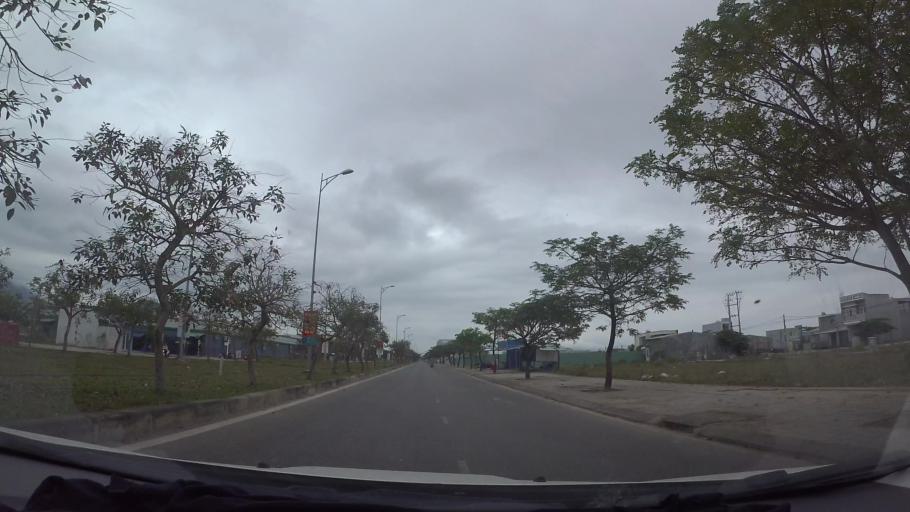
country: VN
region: Da Nang
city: Lien Chieu
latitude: 16.1017
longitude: 108.1188
